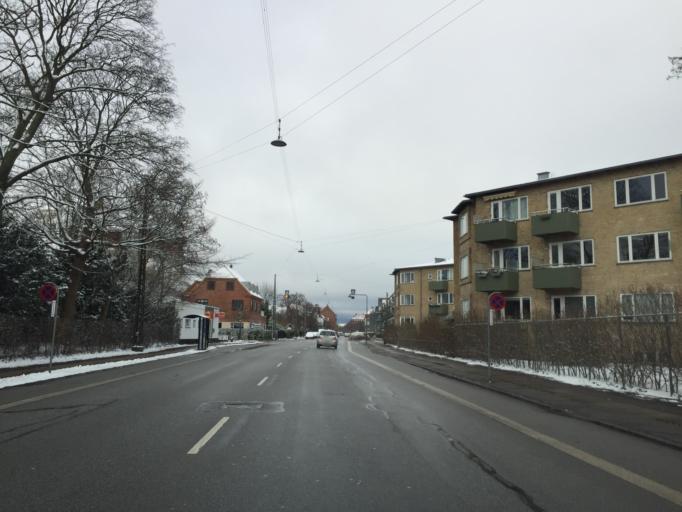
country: DK
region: Capital Region
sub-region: Kobenhavn
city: Christianshavn
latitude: 55.6579
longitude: 12.6202
